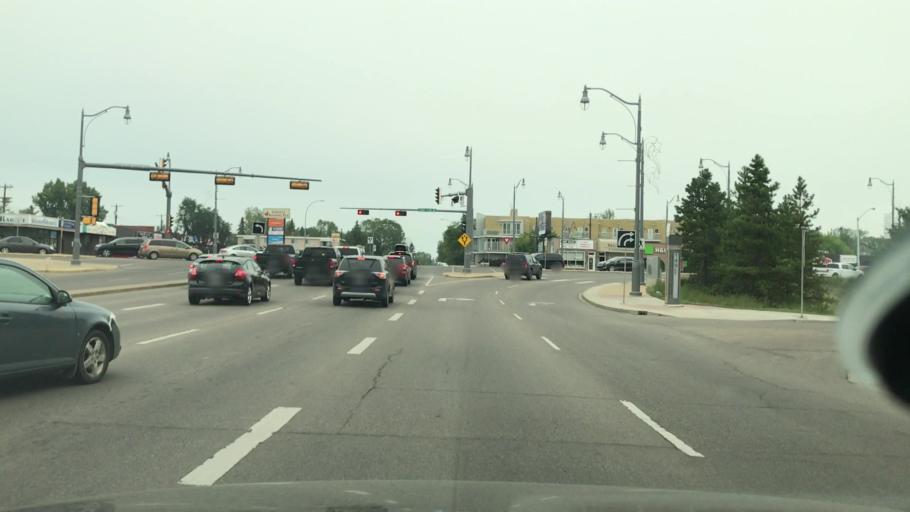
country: CA
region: Alberta
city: St. Albert
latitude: 53.5410
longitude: -113.5779
